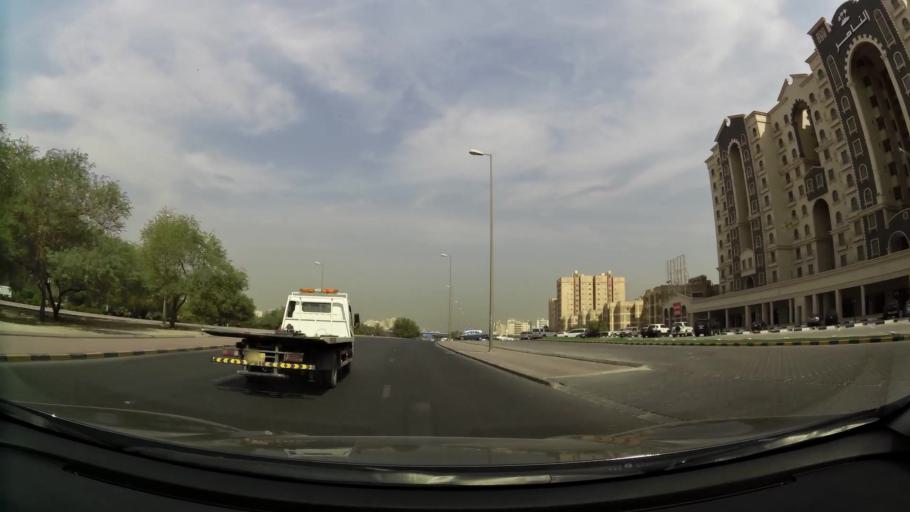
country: KW
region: Al Farwaniyah
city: Al Farwaniyah
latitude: 29.2761
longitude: 47.9694
